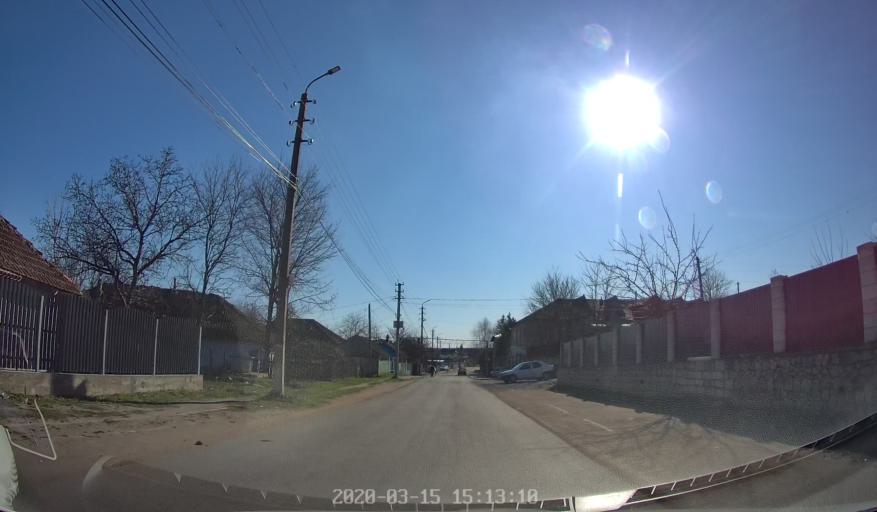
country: MD
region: Orhei
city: Orhei
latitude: 47.2510
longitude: 28.7717
